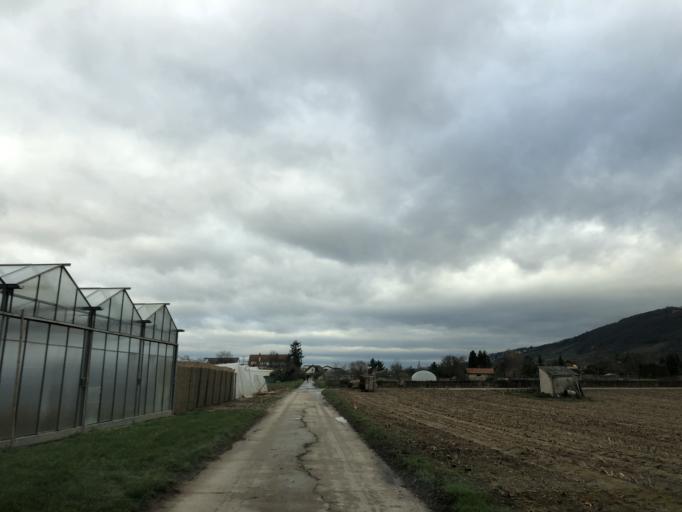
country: DE
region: Baden-Wuerttemberg
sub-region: Karlsruhe Region
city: Dossenheim
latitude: 49.4467
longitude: 8.6620
